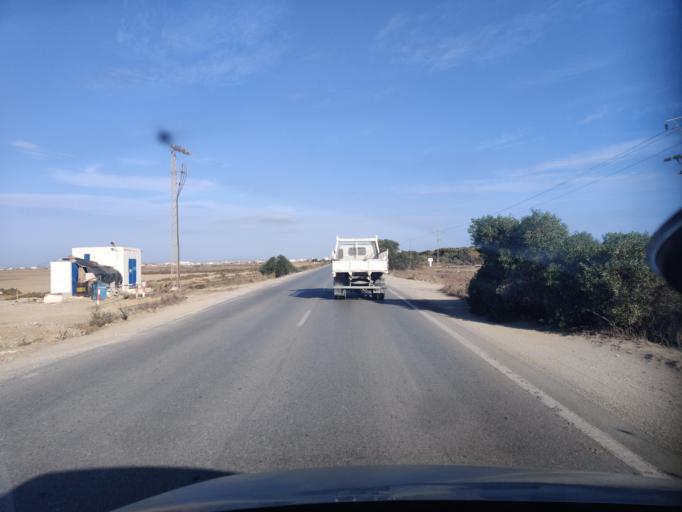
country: TN
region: Ariana
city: Ariana
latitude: 36.9426
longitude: 10.2468
